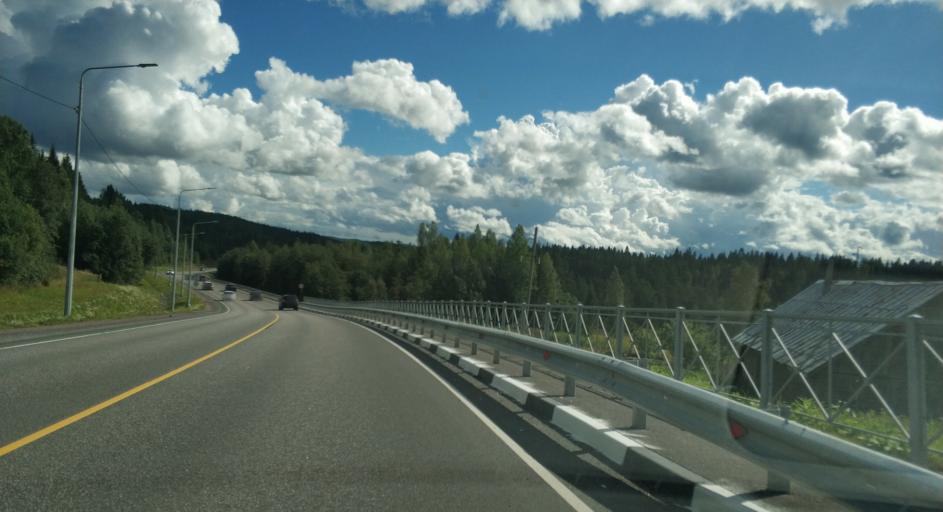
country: RU
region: Republic of Karelia
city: Ruskeala
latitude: 61.9225
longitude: 30.6075
